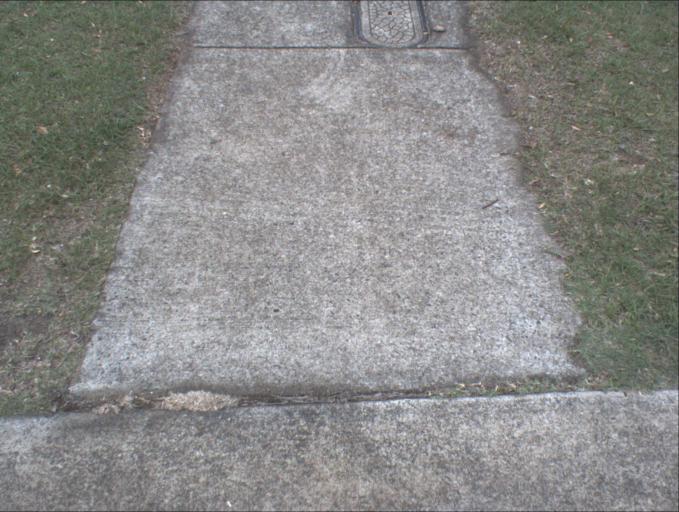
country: AU
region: Queensland
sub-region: Brisbane
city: Sunnybank Hills
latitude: -27.6606
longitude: 153.0194
